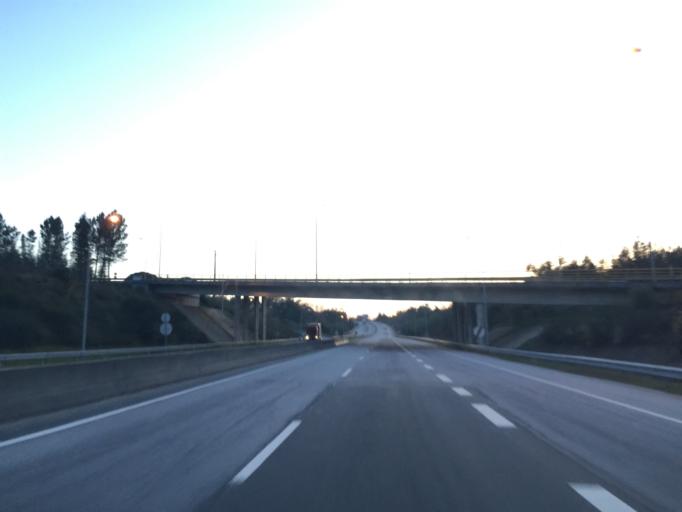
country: PT
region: Viseu
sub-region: Concelho de Carregal do Sal
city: Carregal do Sal
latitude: 40.4308
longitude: -8.0182
